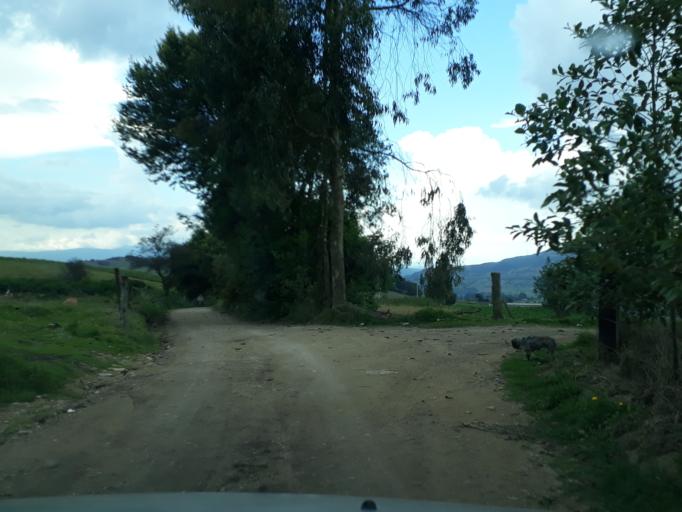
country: CO
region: Cundinamarca
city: Lenguazaque
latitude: 5.2388
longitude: -73.6741
